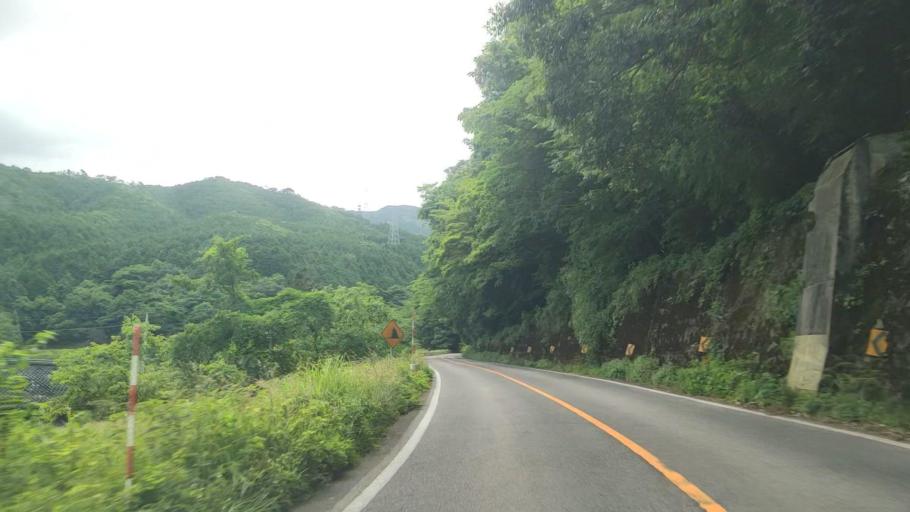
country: JP
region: Tottori
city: Yonago
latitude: 35.2840
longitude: 133.4260
